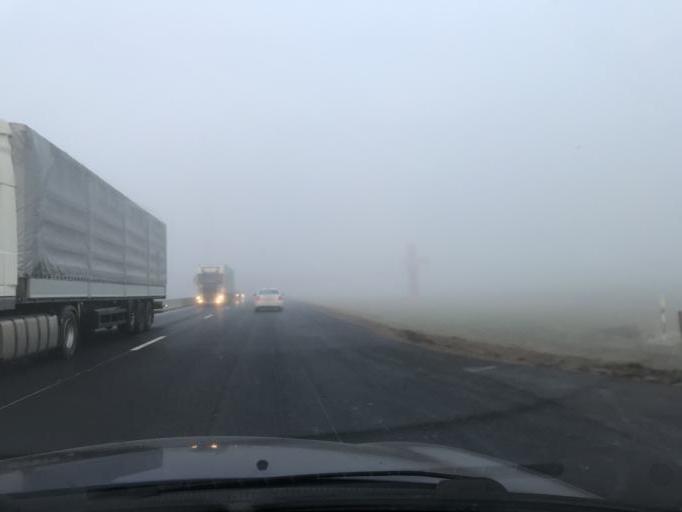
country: BY
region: Minsk
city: Valozhyn
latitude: 54.0446
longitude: 26.5701
